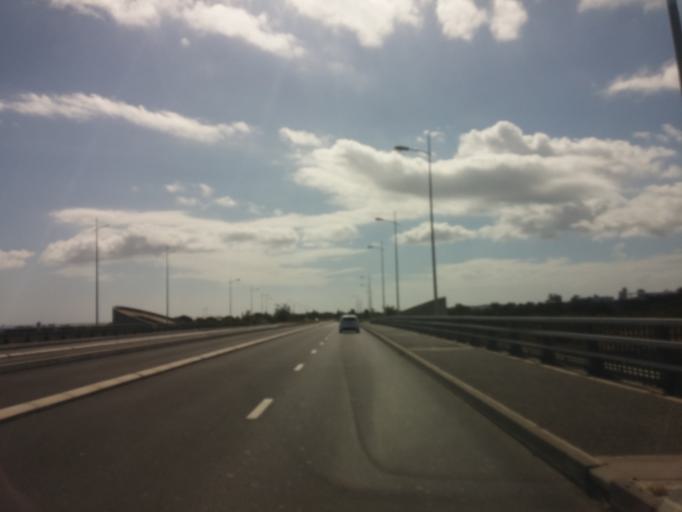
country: RE
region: Reunion
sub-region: Reunion
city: Le Port
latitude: -20.9575
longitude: 55.2939
